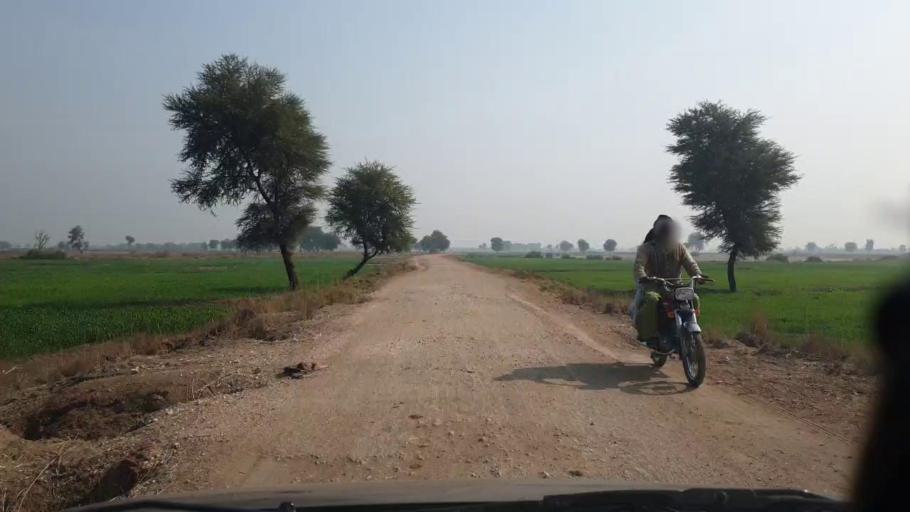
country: PK
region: Sindh
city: Shahdadpur
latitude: 26.0395
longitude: 68.4963
